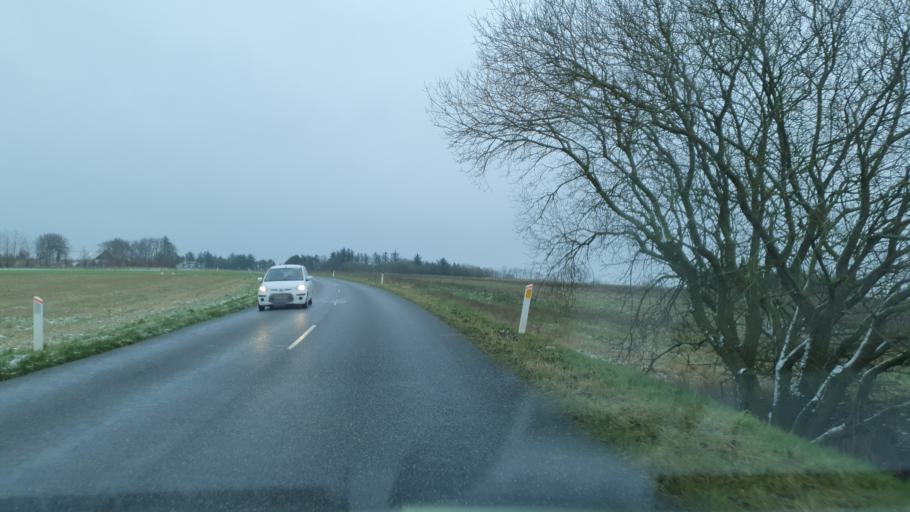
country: DK
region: North Denmark
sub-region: Jammerbugt Kommune
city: Brovst
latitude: 57.1272
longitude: 9.4753
